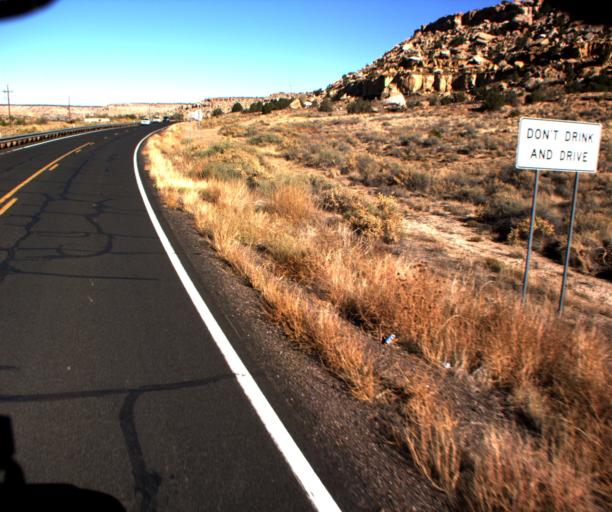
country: US
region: Arizona
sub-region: Navajo County
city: First Mesa
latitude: 35.8182
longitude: -110.2164
